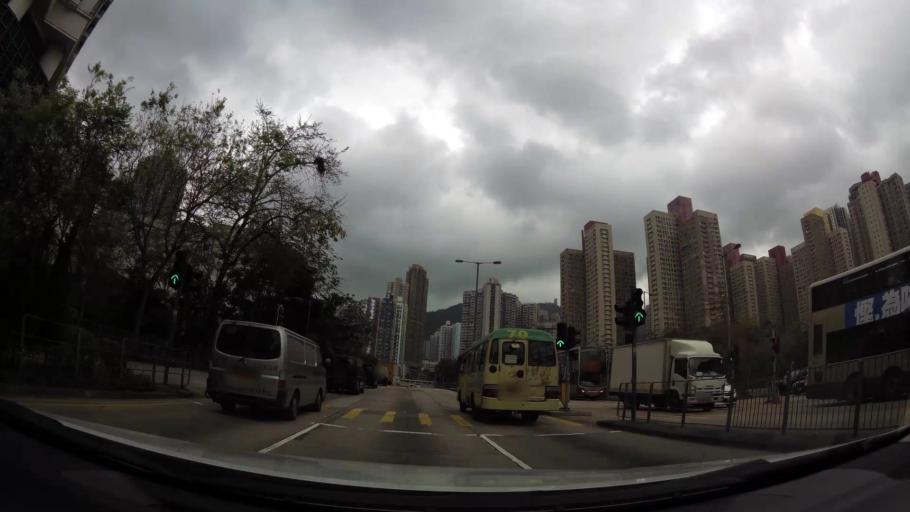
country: HK
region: Wong Tai Sin
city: Wong Tai Sin
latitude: 22.3406
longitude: 114.1982
